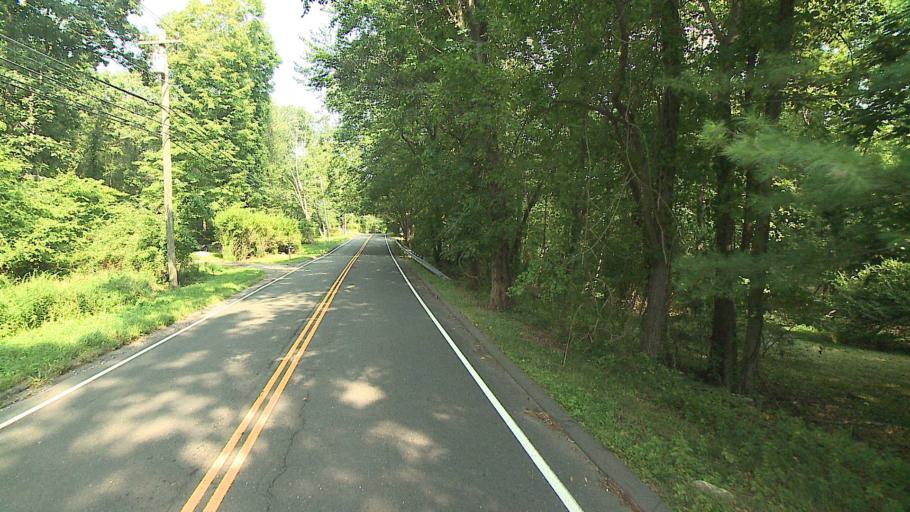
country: US
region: Connecticut
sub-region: Fairfield County
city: Georgetown
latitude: 41.2429
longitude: -73.4116
